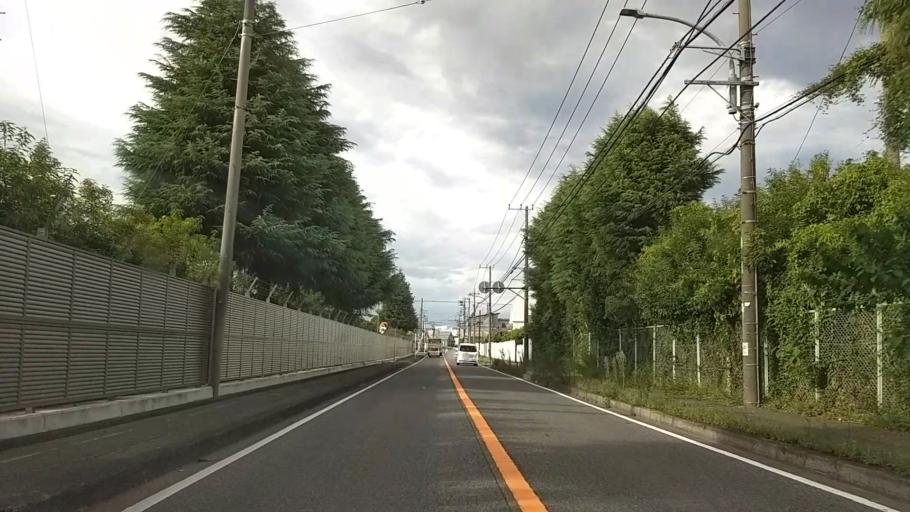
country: JP
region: Kanagawa
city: Zama
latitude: 35.5643
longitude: 139.3402
